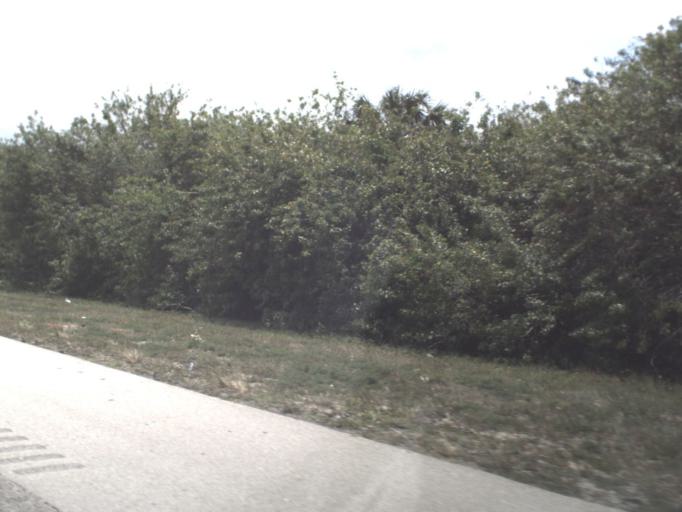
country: US
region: Florida
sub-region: Brevard County
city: Rockledge
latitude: 28.2711
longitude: -80.7305
